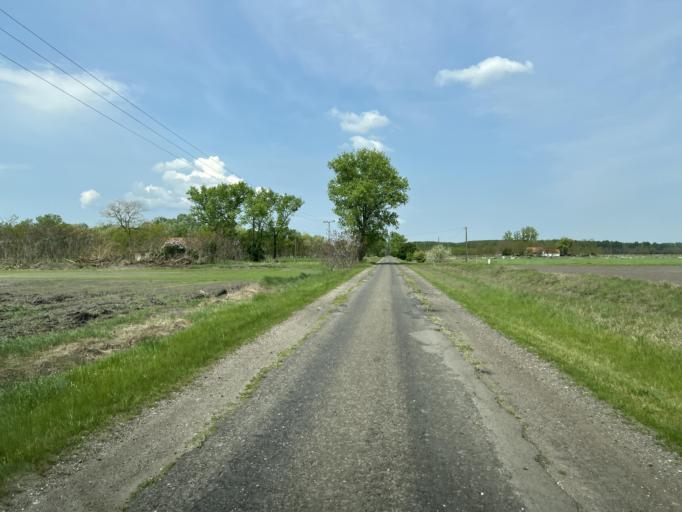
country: HU
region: Pest
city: Kocser
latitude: 47.0423
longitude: 19.9386
